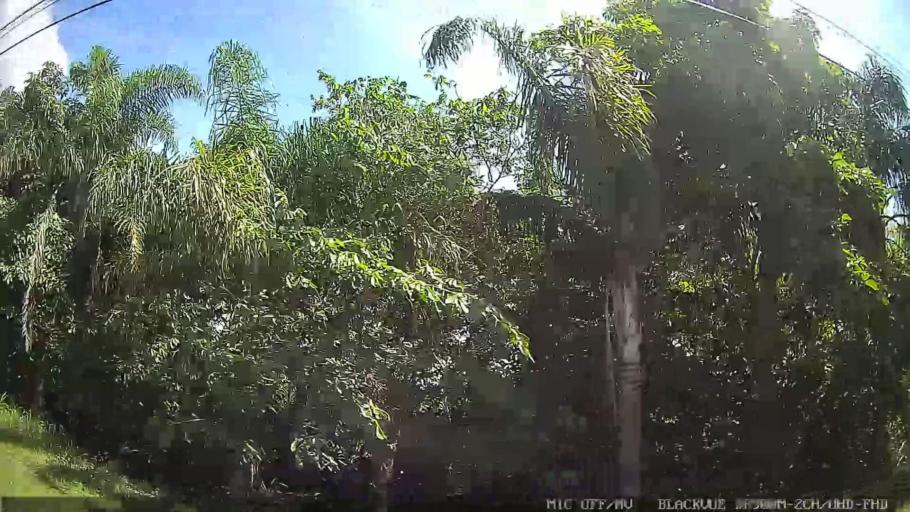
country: BR
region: Sao Paulo
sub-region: Peruibe
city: Peruibe
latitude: -24.3305
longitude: -47.0049
